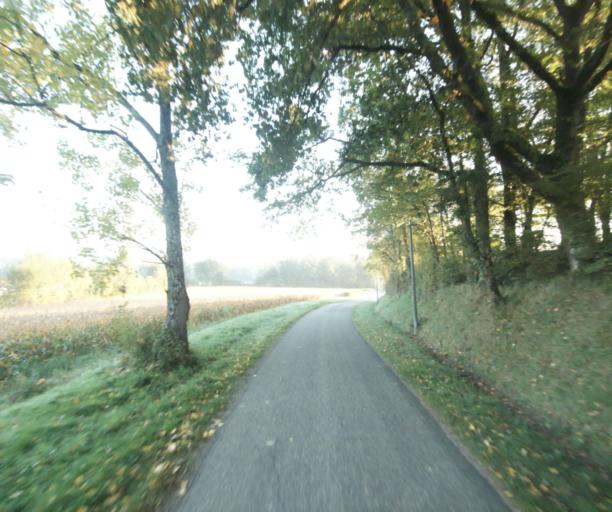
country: FR
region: Midi-Pyrenees
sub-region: Departement du Gers
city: Eauze
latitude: 43.7709
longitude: 0.1692
